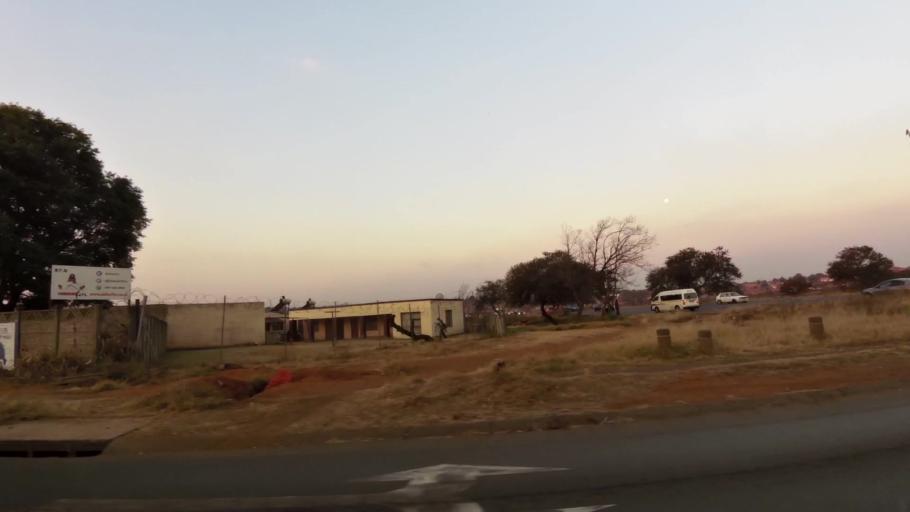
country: ZA
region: Gauteng
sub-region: City of Johannesburg Metropolitan Municipality
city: Soweto
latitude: -26.2914
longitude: 27.8806
